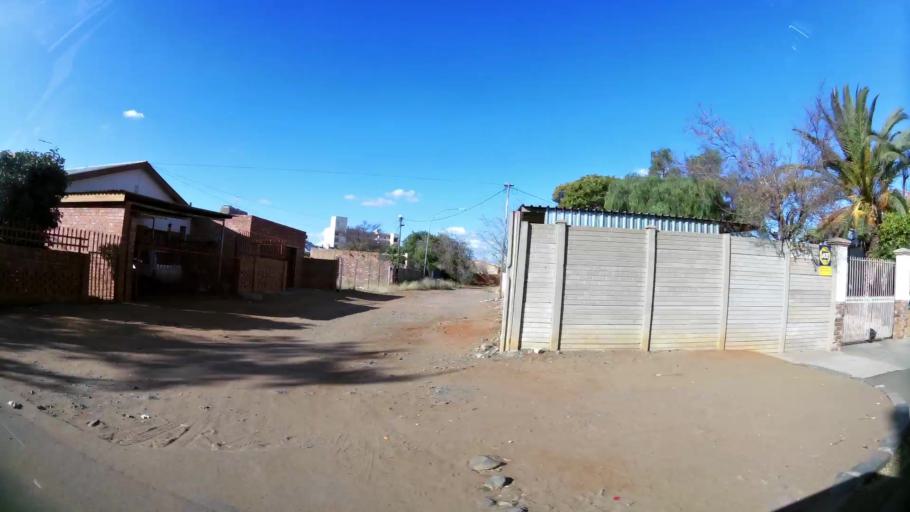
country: ZA
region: Northern Cape
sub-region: Frances Baard District Municipality
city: Kimberley
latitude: -28.7464
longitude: 24.7617
